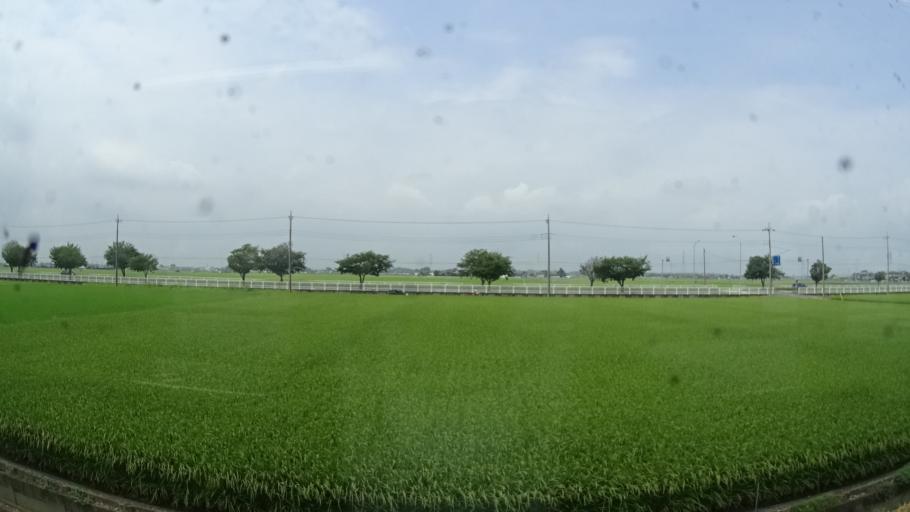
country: JP
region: Ibaraki
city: Shimodate
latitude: 36.3336
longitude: 139.9720
